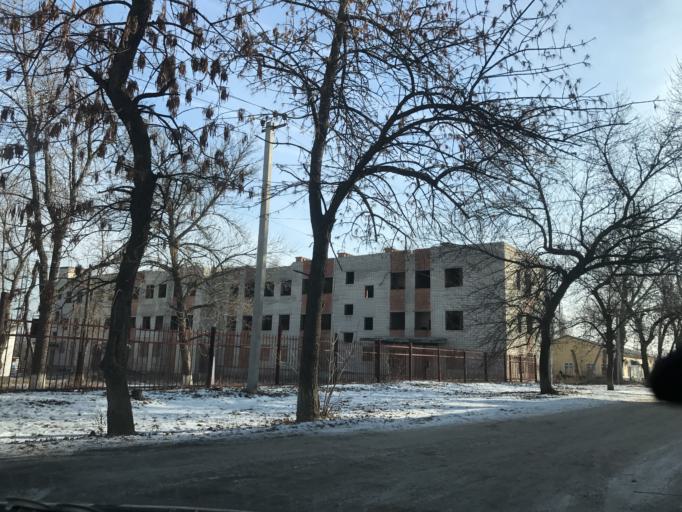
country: RU
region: Rostov
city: Kamensk-Shakhtinskiy
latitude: 48.3250
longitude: 40.2484
